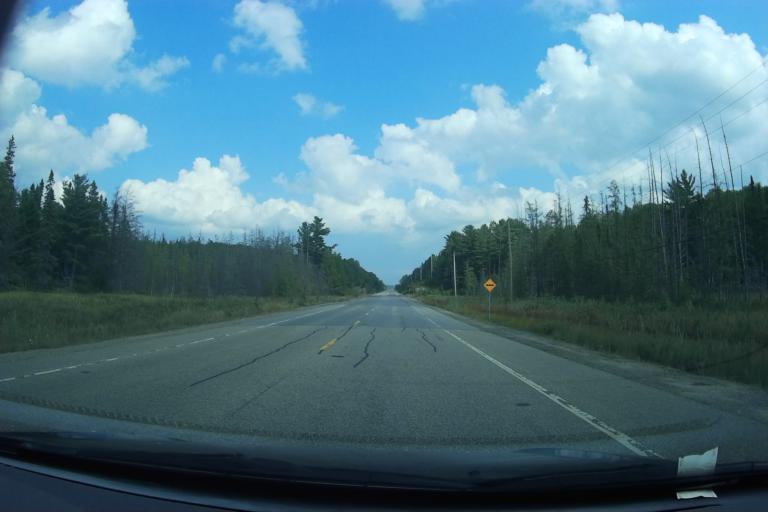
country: CA
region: Ontario
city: Bancroft
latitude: 45.5907
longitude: -78.3575
